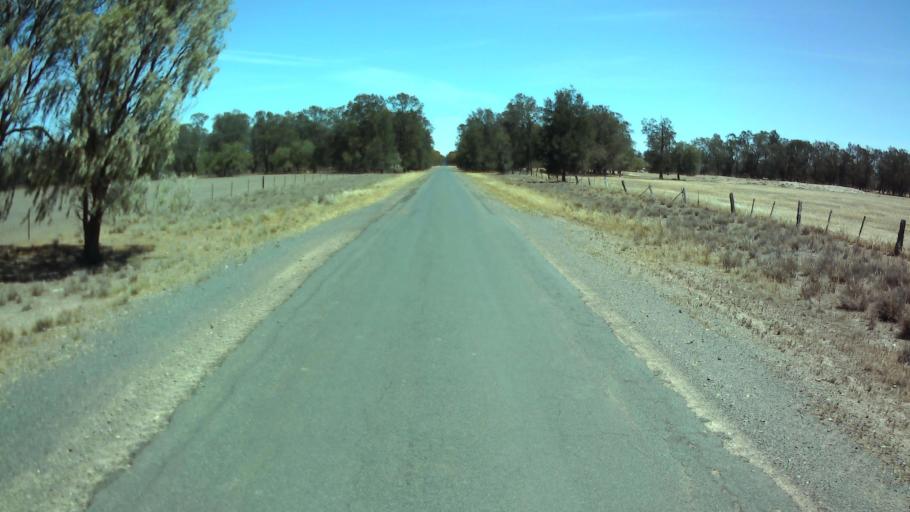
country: AU
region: New South Wales
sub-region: Weddin
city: Grenfell
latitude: -33.8664
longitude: 147.6927
